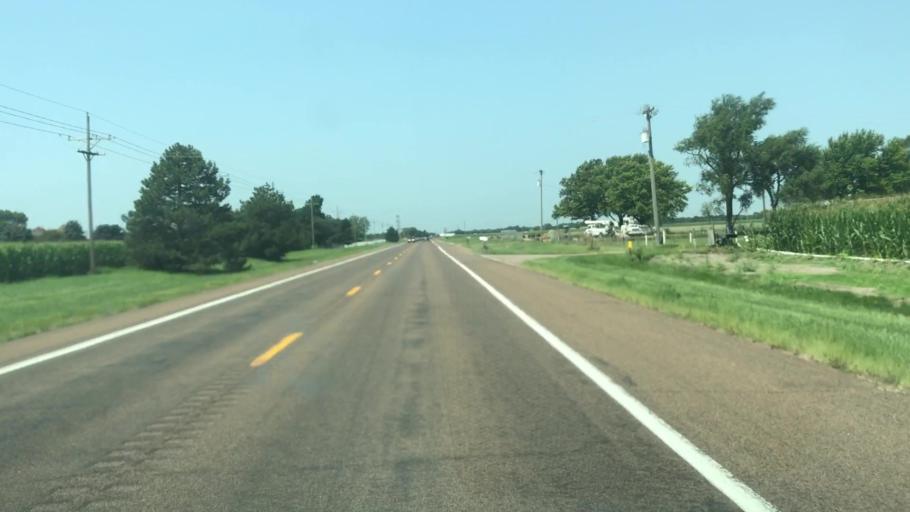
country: US
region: Nebraska
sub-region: Hall County
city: Grand Island
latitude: 40.8869
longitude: -98.3090
